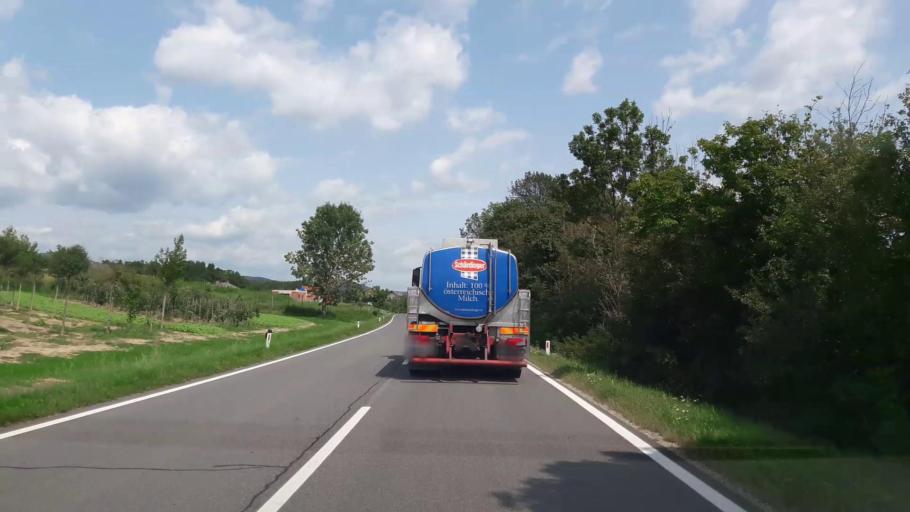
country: AT
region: Styria
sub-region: Politischer Bezirk Hartberg-Fuerstenfeld
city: Kaindorf
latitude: 47.2335
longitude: 15.9195
